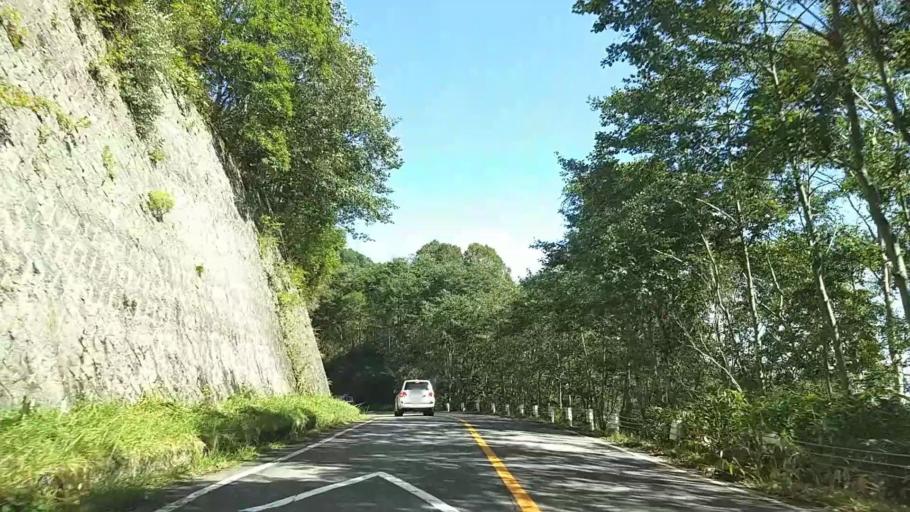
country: JP
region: Nagano
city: Suwa
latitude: 36.1708
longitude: 138.1303
